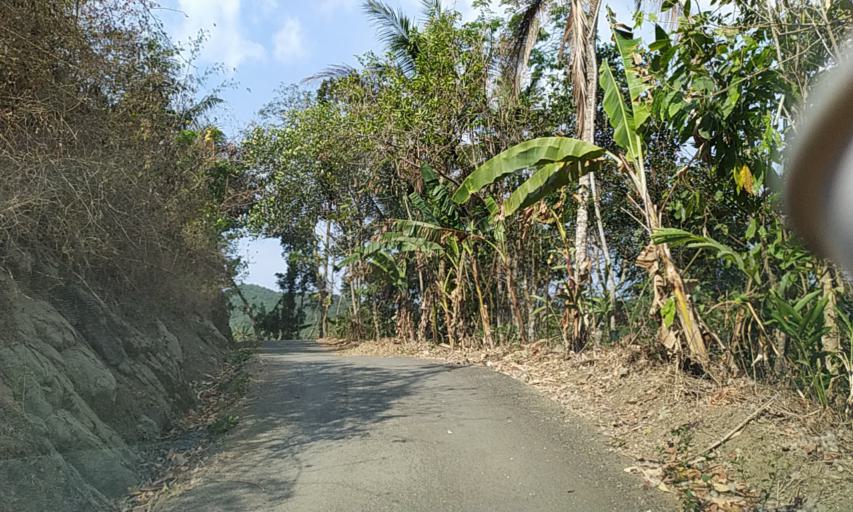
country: ID
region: Central Java
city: Jambuluwuk
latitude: -7.3219
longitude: 108.9058
